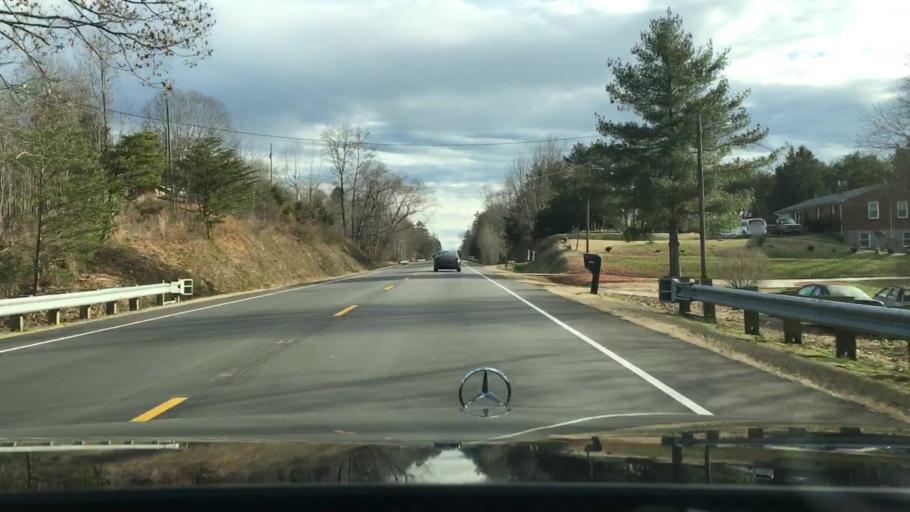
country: US
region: North Carolina
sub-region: Caswell County
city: Yanceyville
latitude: 36.4566
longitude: -79.3702
